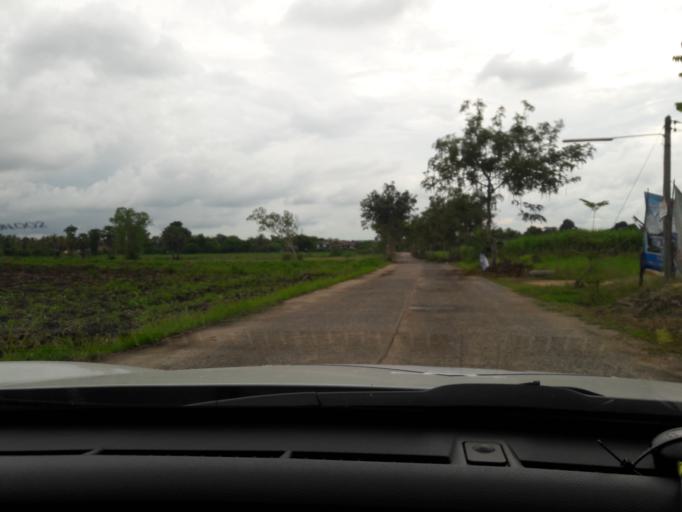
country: TH
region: Nakhon Sawan
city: Tak Fa
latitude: 15.3557
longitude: 100.5006
